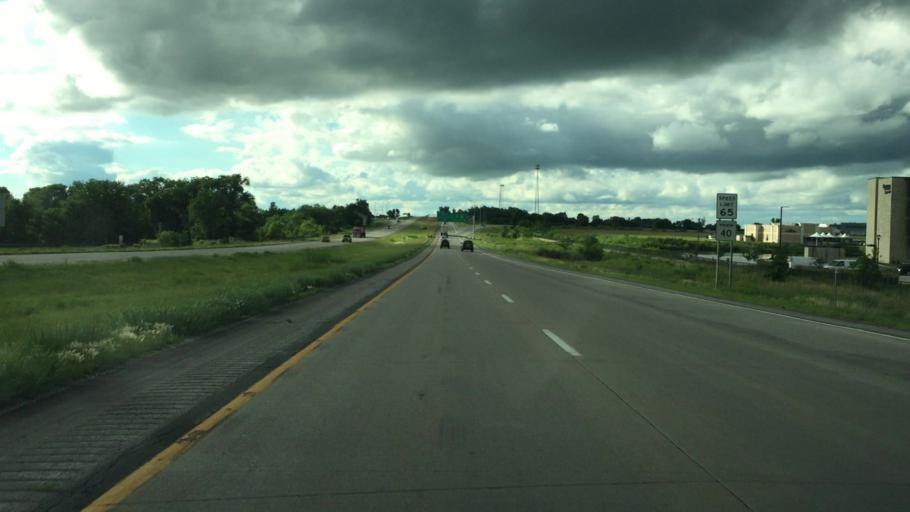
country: US
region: Iowa
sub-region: Polk County
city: Altoona
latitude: 41.6518
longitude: -93.5157
